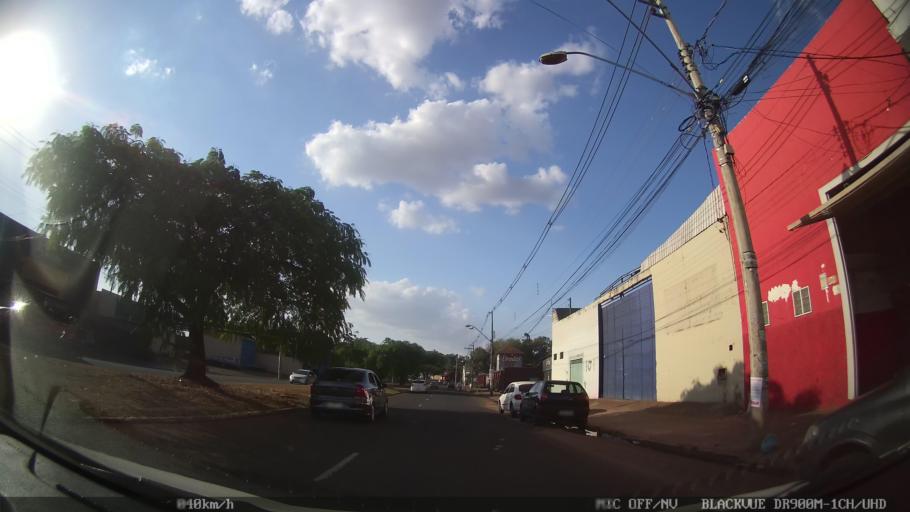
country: BR
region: Sao Paulo
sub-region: Ribeirao Preto
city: Ribeirao Preto
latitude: -21.1476
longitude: -47.8003
